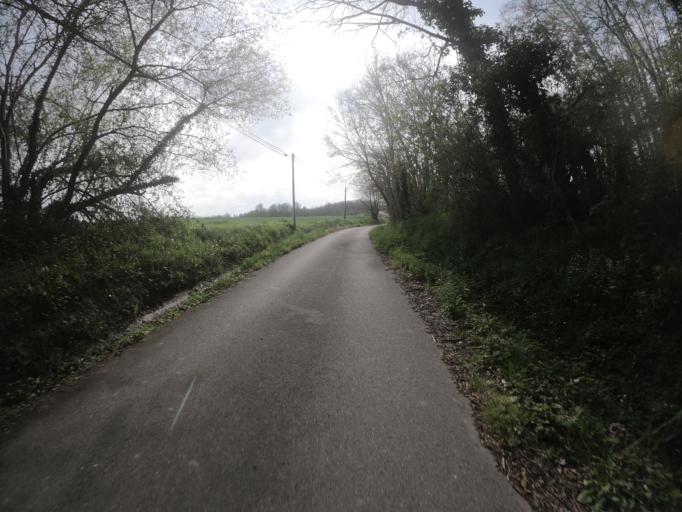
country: FR
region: Midi-Pyrenees
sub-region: Departement de l'Ariege
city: La Tour-du-Crieu
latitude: 43.1015
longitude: 1.7211
